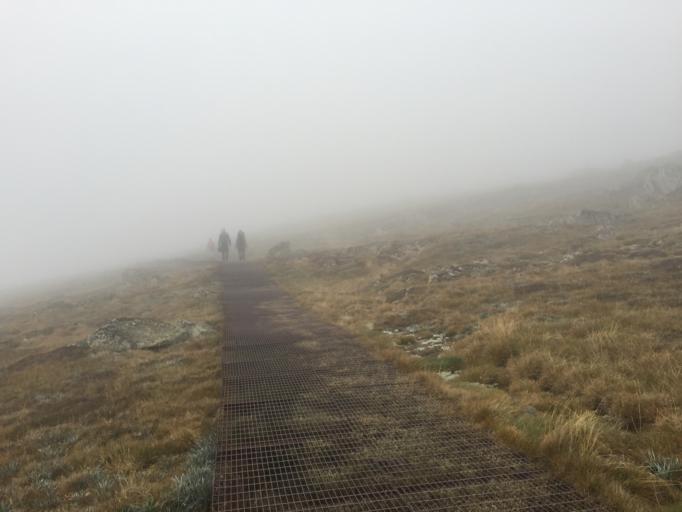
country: AU
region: New South Wales
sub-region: Snowy River
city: Jindabyne
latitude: -36.4638
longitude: 148.2699
